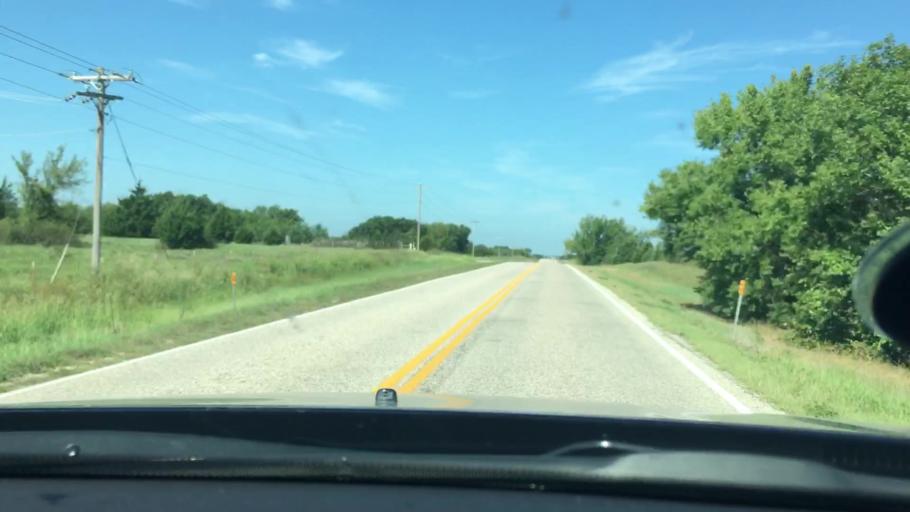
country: US
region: Oklahoma
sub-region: Johnston County
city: Tishomingo
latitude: 34.3614
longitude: -96.5587
